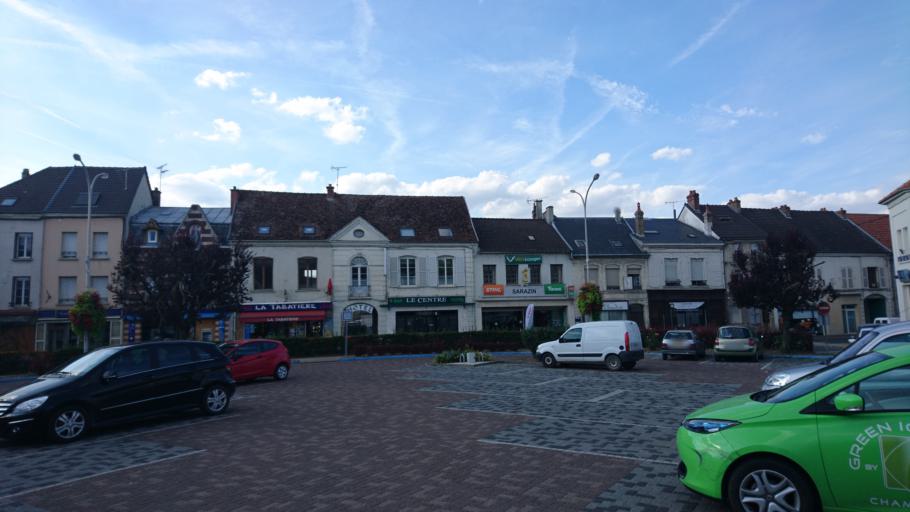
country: FR
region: Champagne-Ardenne
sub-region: Departement de la Marne
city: Dormans
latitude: 49.0766
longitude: 3.6410
